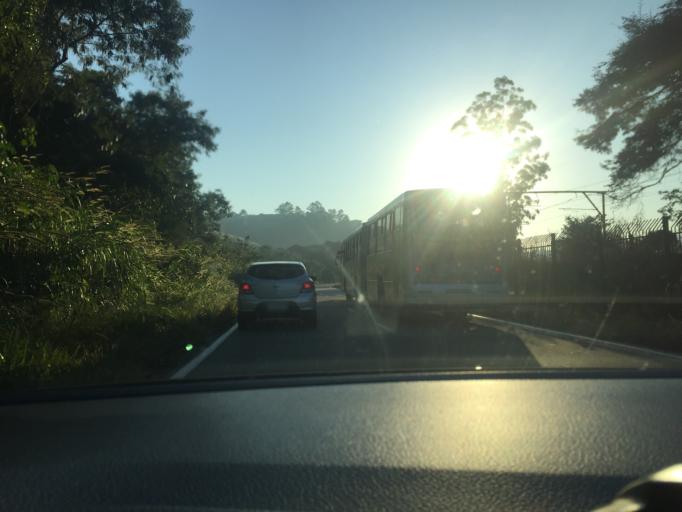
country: BR
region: Sao Paulo
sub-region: Varzea Paulista
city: Varzea Paulista
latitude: -23.2030
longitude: -46.8202
